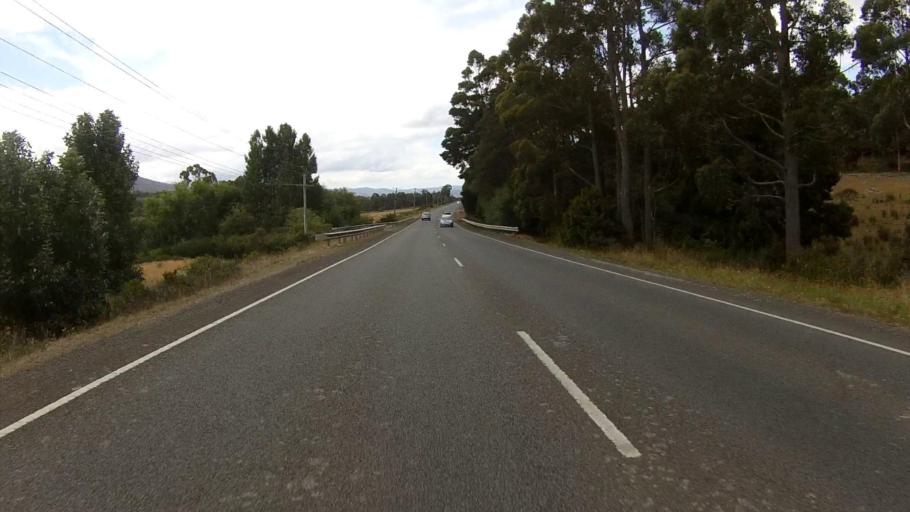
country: AU
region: Tasmania
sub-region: Kingborough
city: Kettering
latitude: -43.0867
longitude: 147.2515
